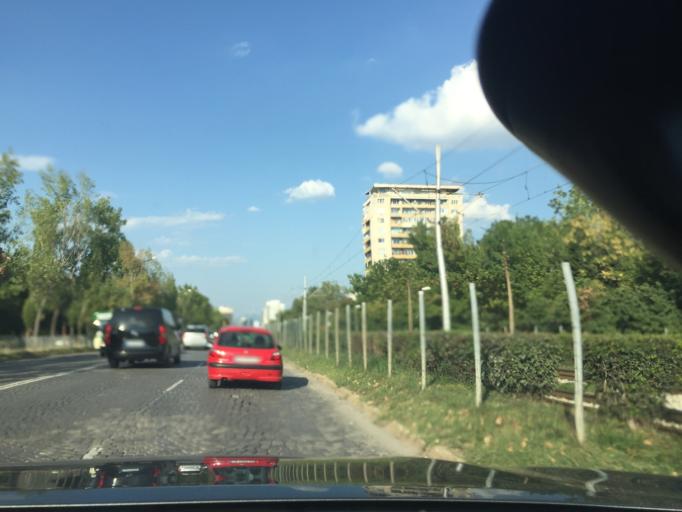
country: BG
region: Sofia-Capital
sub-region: Stolichna Obshtina
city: Sofia
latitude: 42.6816
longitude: 23.2902
